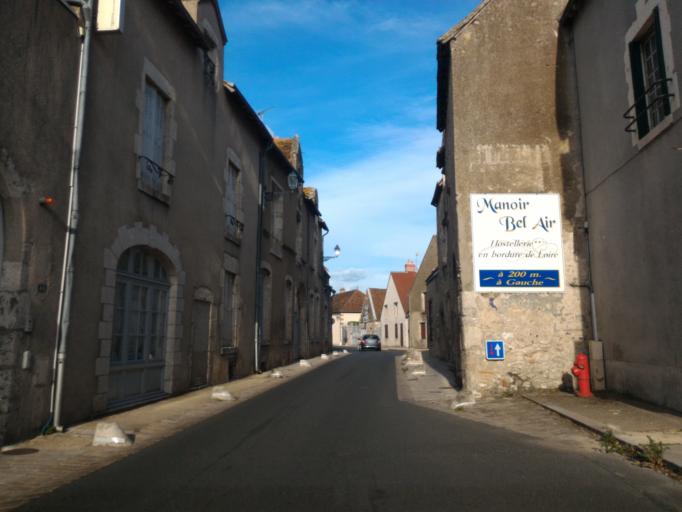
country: FR
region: Centre
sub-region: Departement du Loir-et-Cher
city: Saint-Dye-sur-Loire
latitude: 47.6559
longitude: 1.4892
